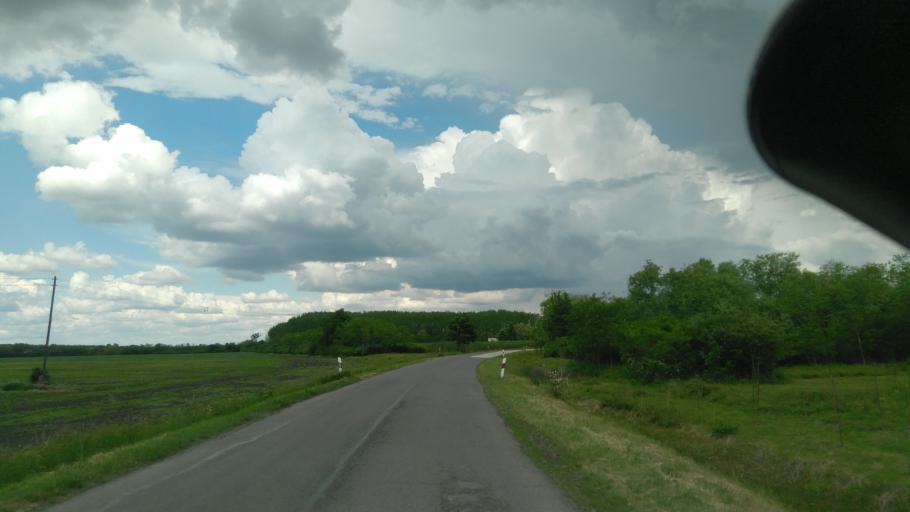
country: HU
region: Bekes
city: Bucsa
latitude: 47.1545
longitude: 21.0685
